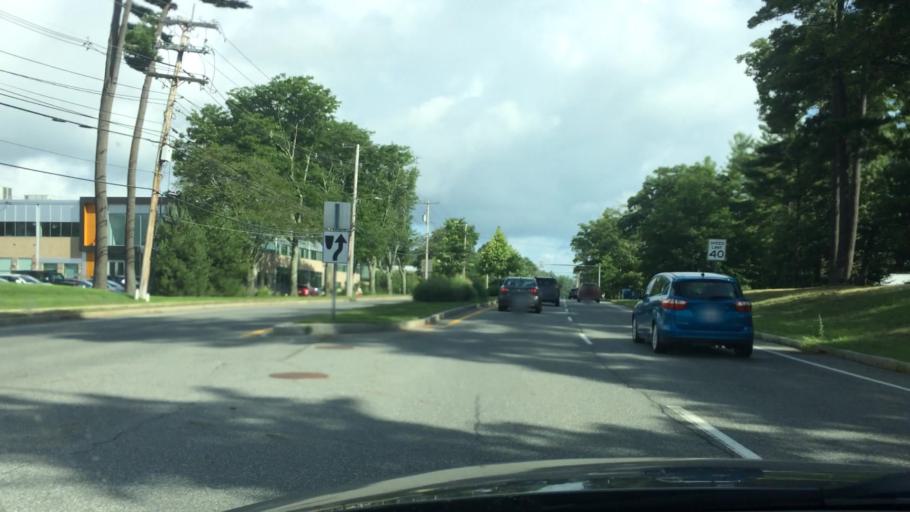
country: US
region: Massachusetts
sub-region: Middlesex County
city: Pinehurst
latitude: 42.5039
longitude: -71.2415
